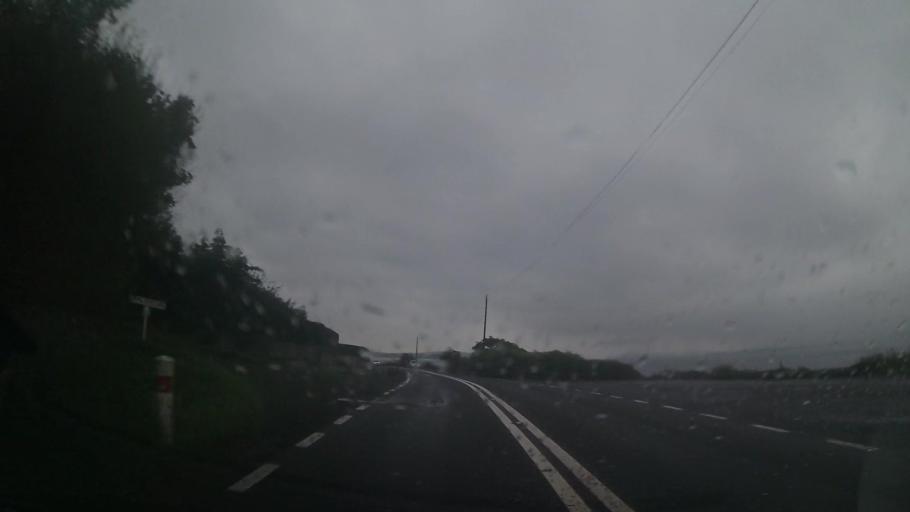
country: GB
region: Scotland
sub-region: North Ayrshire
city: Skelmorlie
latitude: 55.8399
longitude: -4.8921
